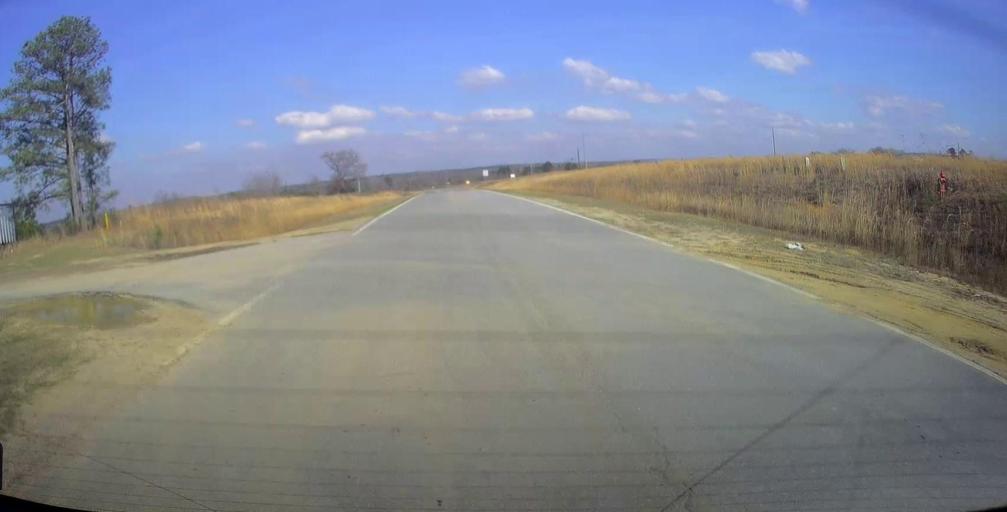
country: US
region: Georgia
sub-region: Wilkinson County
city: Gordon
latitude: 32.8959
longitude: -83.3054
